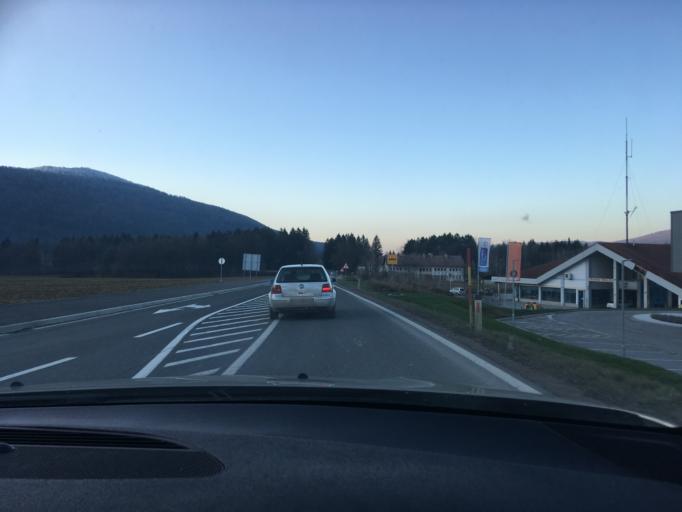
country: SI
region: Kocevje
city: Kocevje
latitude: 45.6531
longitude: 14.8513
